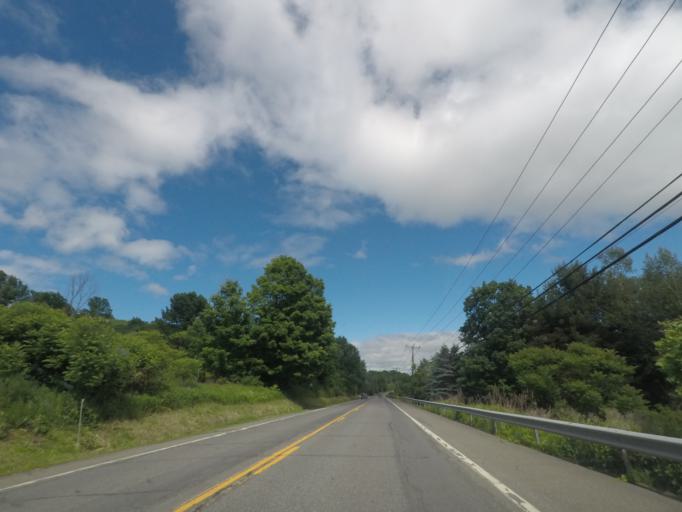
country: US
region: New York
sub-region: Columbia County
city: Philmont
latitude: 42.1821
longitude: -73.5427
